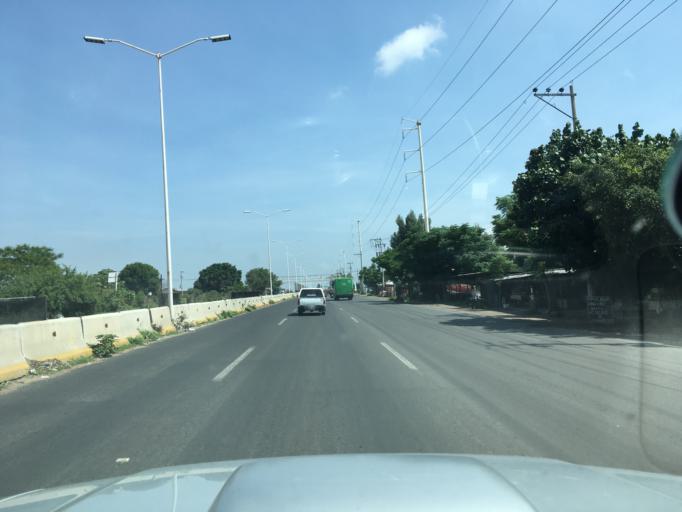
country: MX
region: Jalisco
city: Tonala
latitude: 20.6694
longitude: -103.2351
